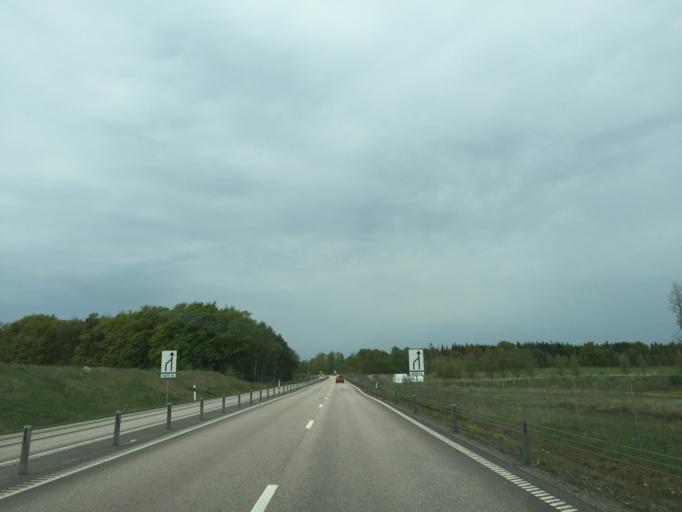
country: SE
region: Skane
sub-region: Helsingborg
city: Helsingborg
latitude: 56.1022
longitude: 12.6641
